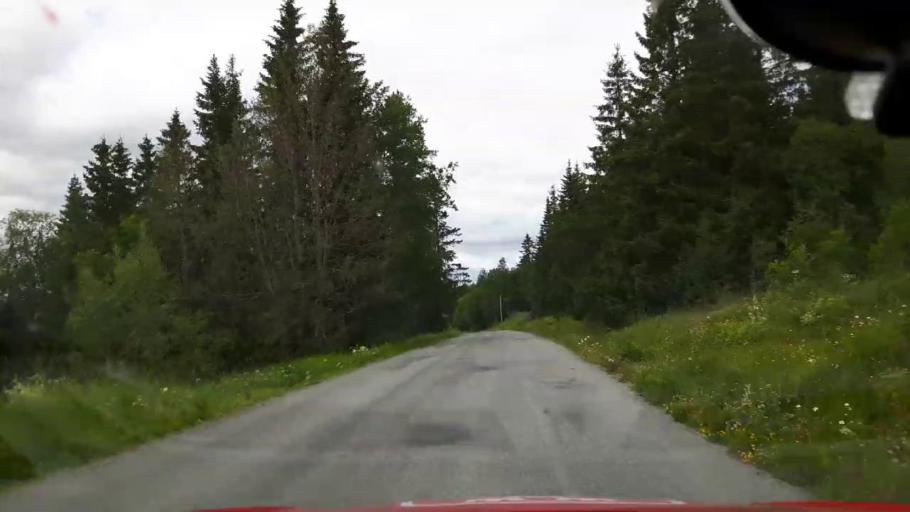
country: SE
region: Jaemtland
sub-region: OEstersunds Kommun
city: Brunflo
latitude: 63.0857
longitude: 14.8444
